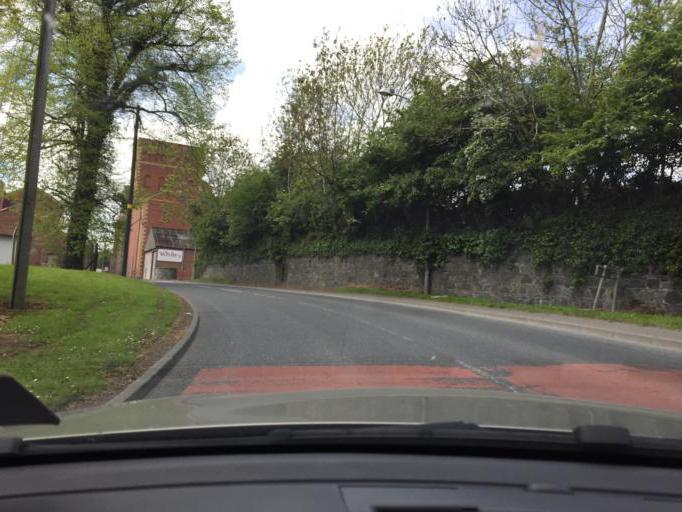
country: GB
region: Northern Ireland
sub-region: Armagh District
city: Tandragee
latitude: 54.3493
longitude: -6.4060
